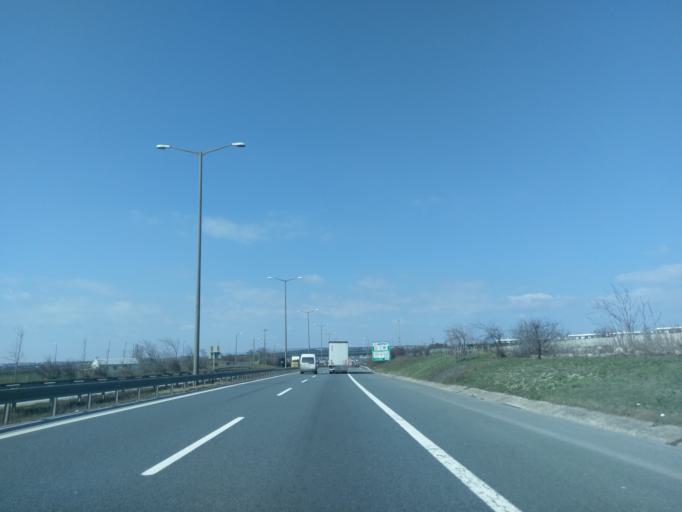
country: TR
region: Istanbul
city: Selimpasa
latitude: 41.0771
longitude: 28.3745
